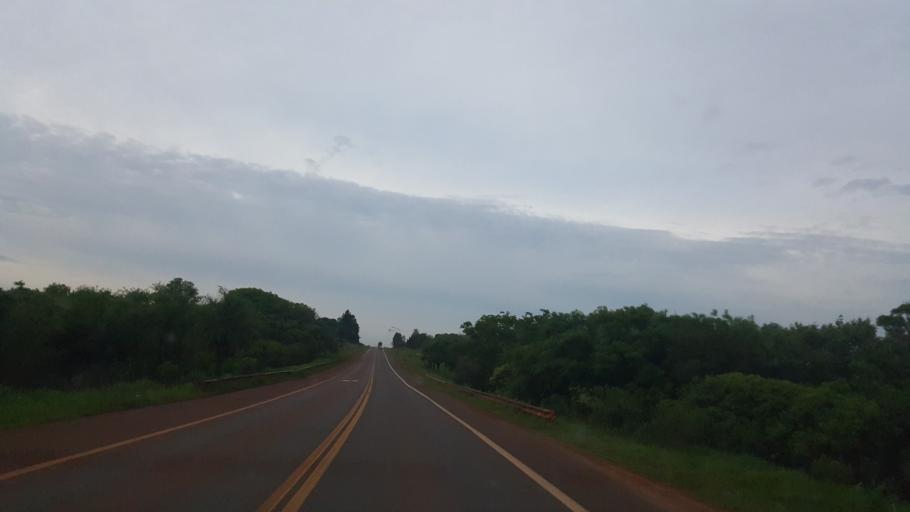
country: AR
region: Misiones
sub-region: Departamento de Apostoles
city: San Jose
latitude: -27.7500
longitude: -55.7848
